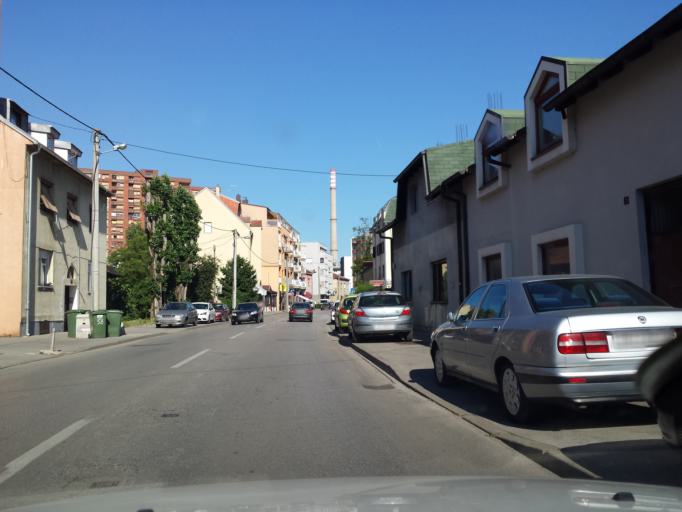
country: HR
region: Grad Zagreb
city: Zagreb - Centar
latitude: 45.8079
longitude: 15.9386
